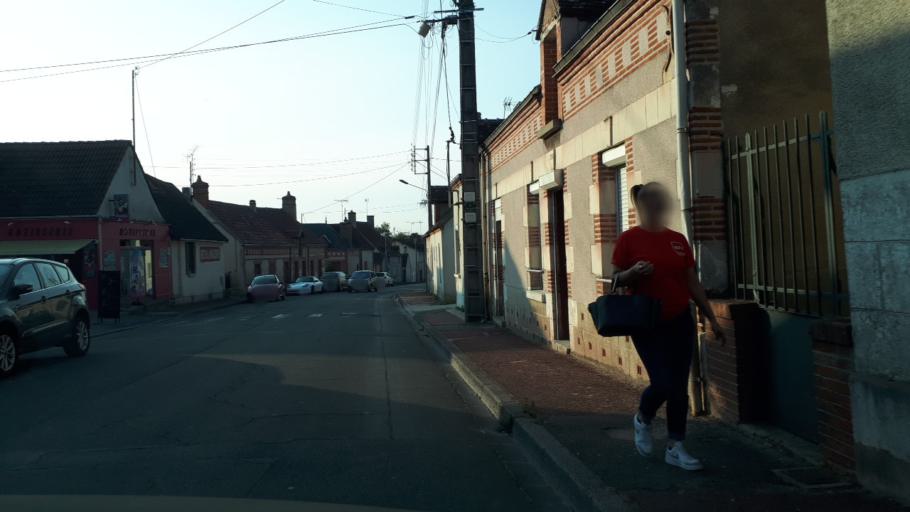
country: FR
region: Centre
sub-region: Departement du Loir-et-Cher
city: Romorantin-Lanthenay
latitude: 47.3621
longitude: 1.7339
